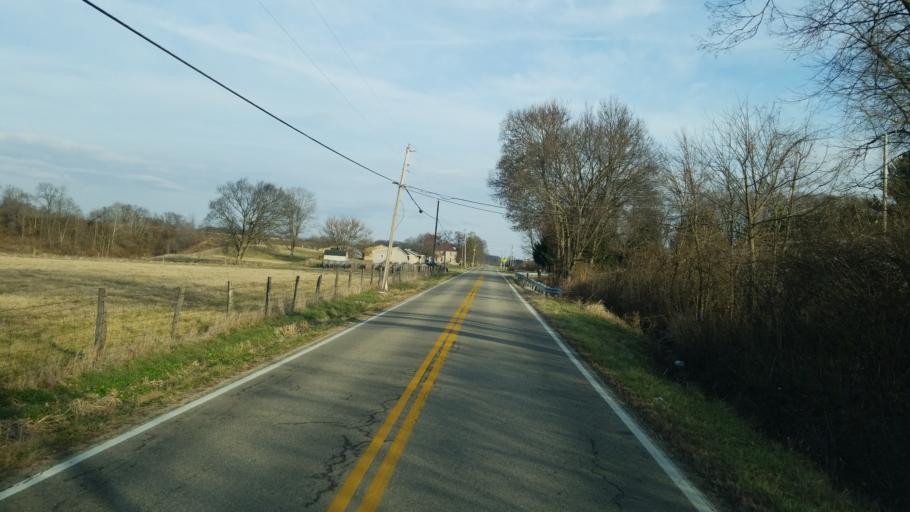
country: US
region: Ohio
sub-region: Ross County
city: Kingston
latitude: 39.4220
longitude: -82.9396
